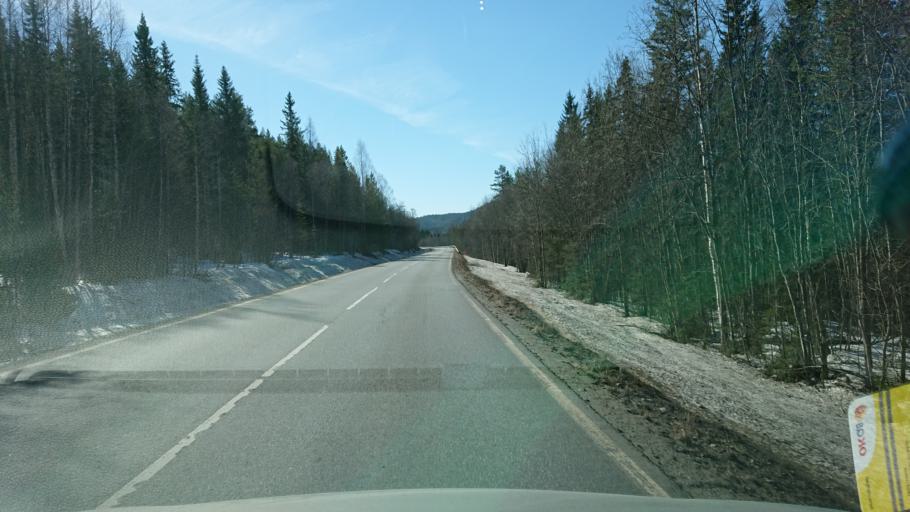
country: SE
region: Vaesterbotten
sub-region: Dorotea Kommun
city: Dorotea
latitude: 64.0466
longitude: 16.2592
